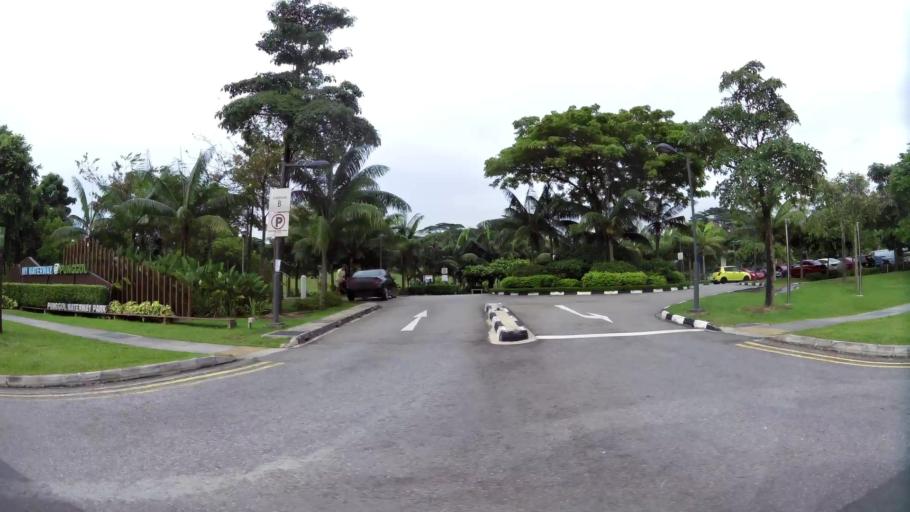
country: MY
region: Johor
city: Kampung Pasir Gudang Baru
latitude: 1.4106
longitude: 103.9044
